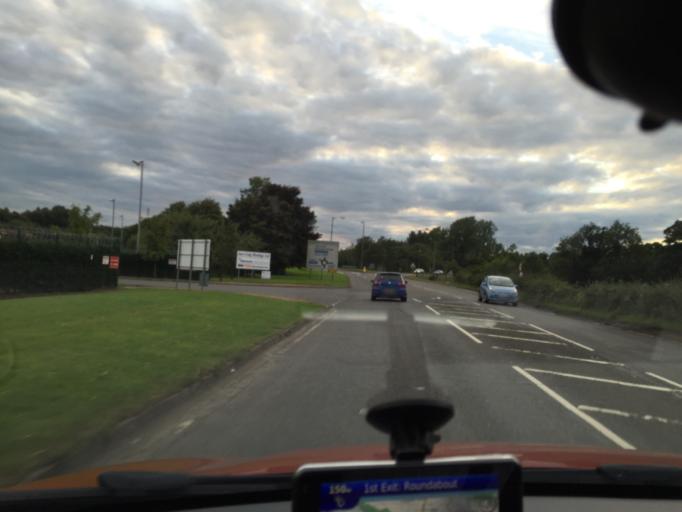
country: GB
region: Scotland
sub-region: Falkirk
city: Bonnybridge
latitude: 56.0124
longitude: -3.8681
